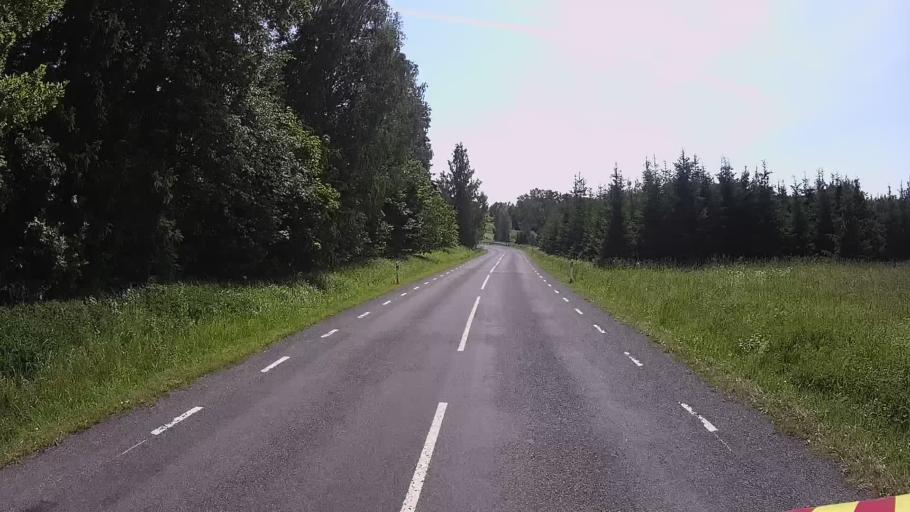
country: EE
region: Viljandimaa
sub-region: Karksi vald
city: Karksi-Nuia
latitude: 58.0775
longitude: 25.5607
